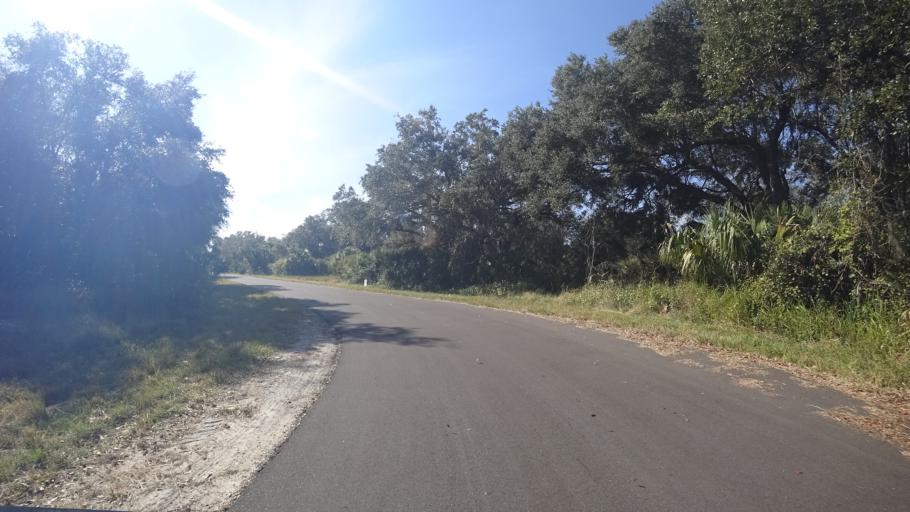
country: US
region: Florida
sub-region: Charlotte County
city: Port Charlotte
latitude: 27.0603
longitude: -82.1210
